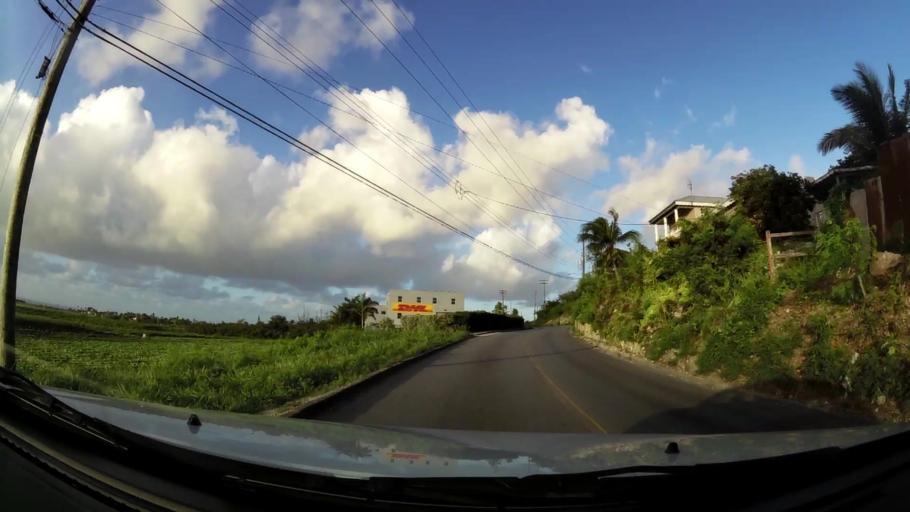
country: BB
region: Christ Church
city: Oistins
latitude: 13.0788
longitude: -59.5066
